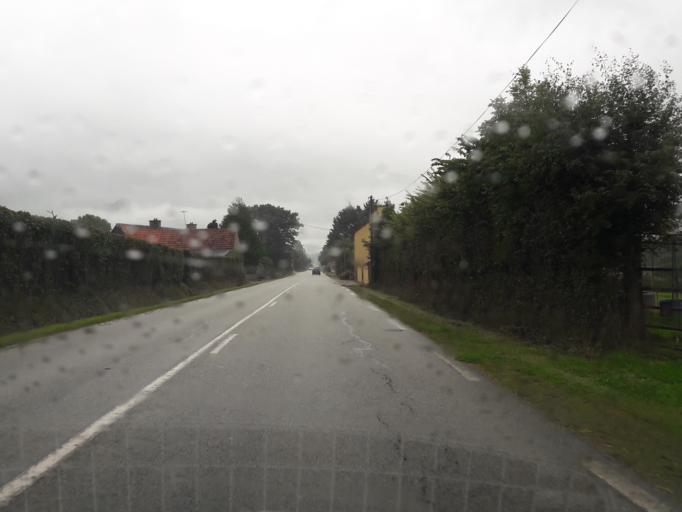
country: FR
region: Lower Normandy
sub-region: Departement de la Manche
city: Martinvast
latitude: 49.5650
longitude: -1.7336
